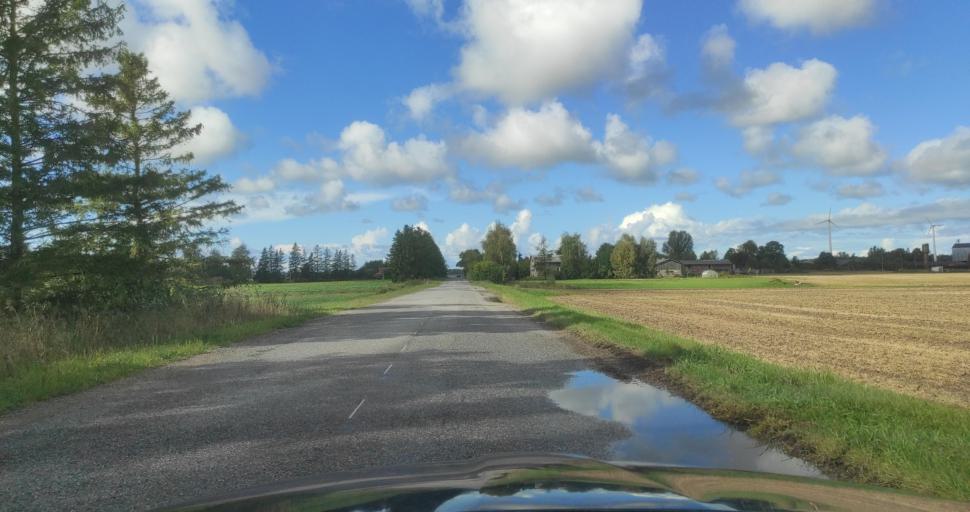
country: LV
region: Ventspils Rajons
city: Piltene
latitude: 57.2637
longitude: 21.5958
